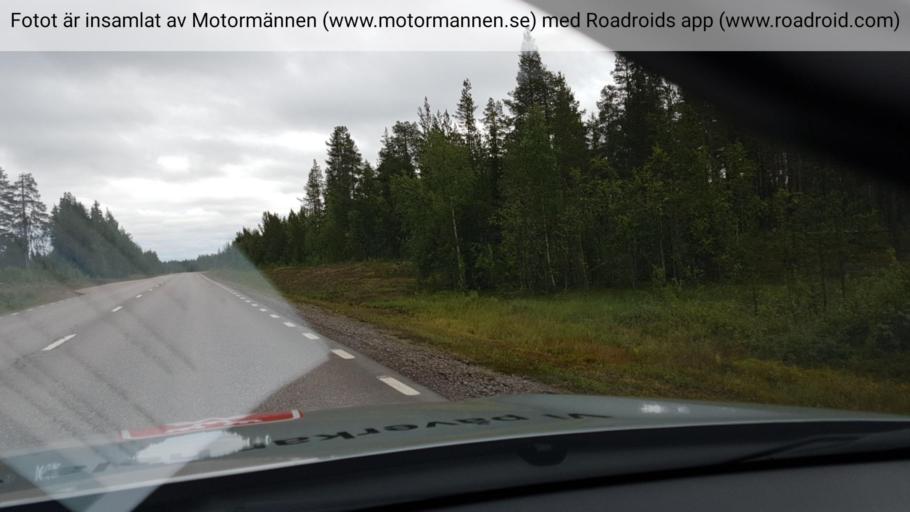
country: SE
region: Norrbotten
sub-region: Gallivare Kommun
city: Gaellivare
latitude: 67.0710
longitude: 21.1096
